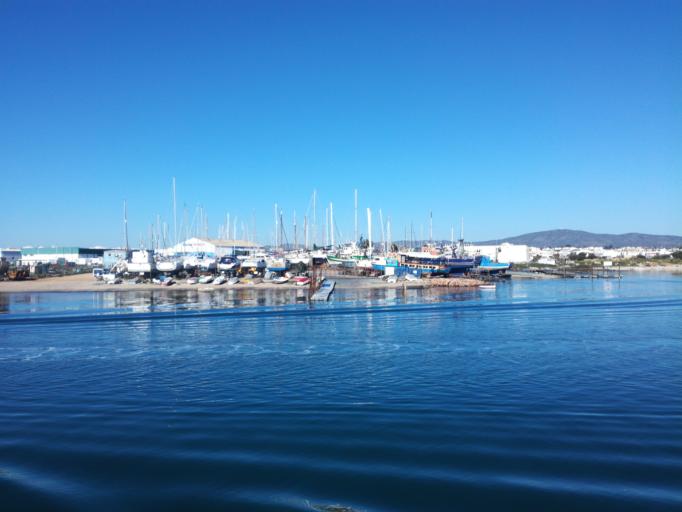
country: PT
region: Faro
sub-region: Olhao
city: Olhao
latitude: 37.0255
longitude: -7.8272
